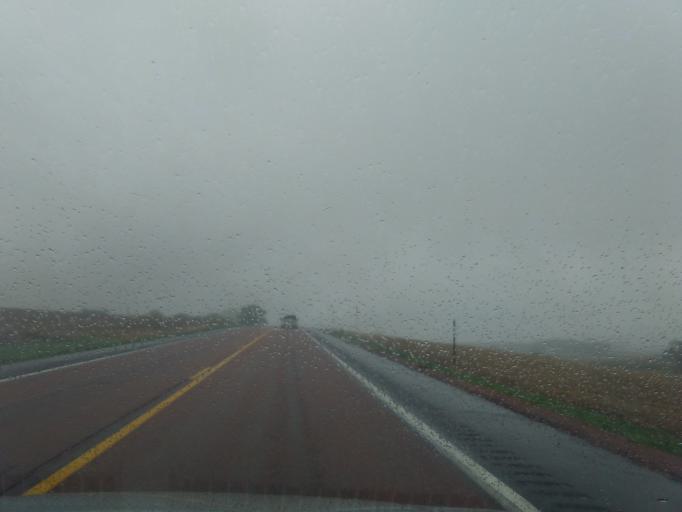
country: US
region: Nebraska
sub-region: Wayne County
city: Wayne
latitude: 42.2356
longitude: -97.1305
